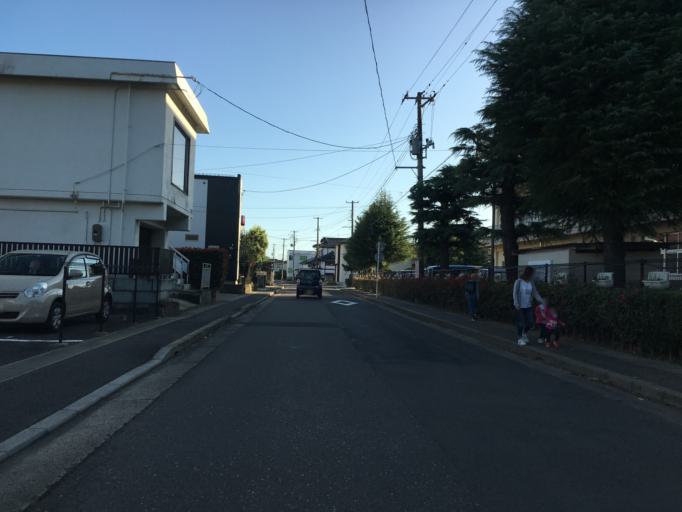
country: JP
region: Fukushima
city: Koriyama
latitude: 37.4029
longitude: 140.3462
